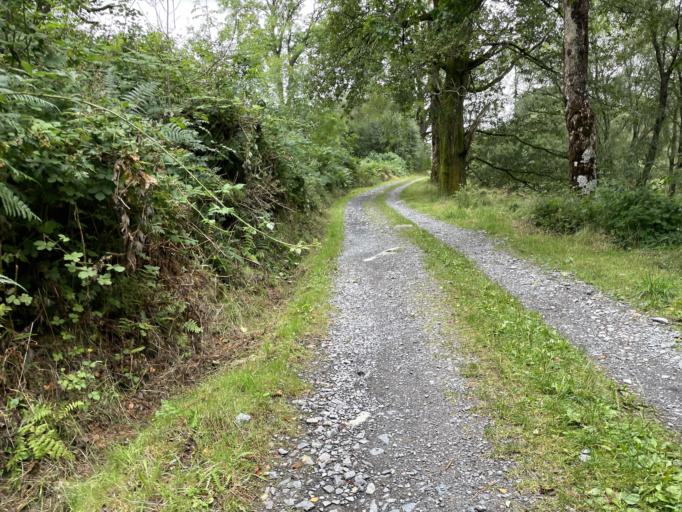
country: GB
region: Scotland
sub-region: Dumfries and Galloway
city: Newton Stewart
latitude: 55.0905
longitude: -4.4608
